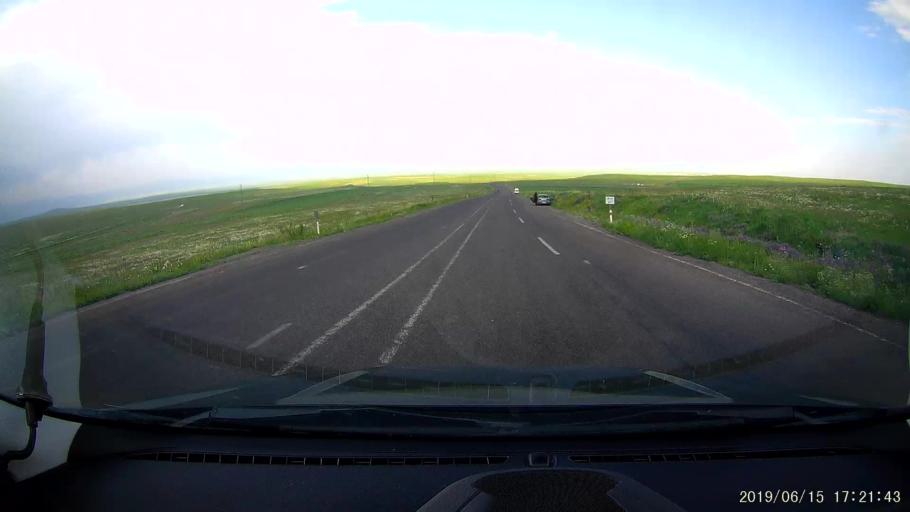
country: TR
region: Kars
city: Basgedikler
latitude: 40.6170
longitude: 43.3300
